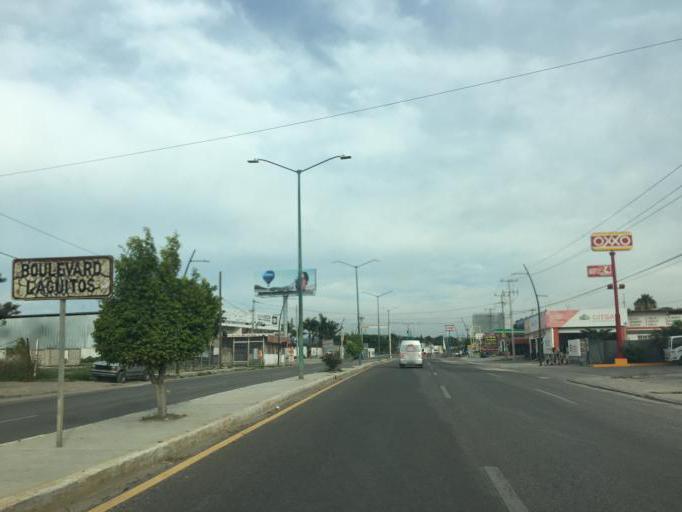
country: MX
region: Chiapas
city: Tuxtla Gutierrez
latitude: 16.7661
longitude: -93.1649
